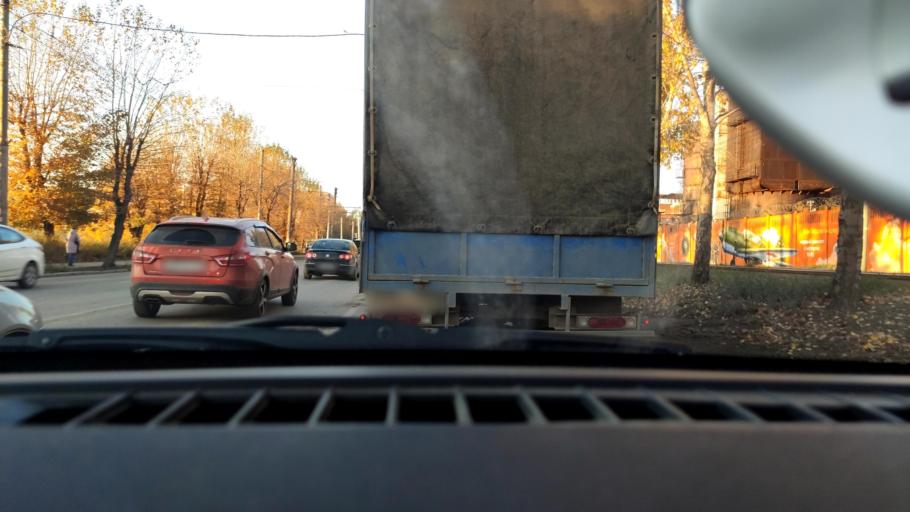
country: RU
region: Perm
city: Perm
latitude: 57.9809
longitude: 56.2487
